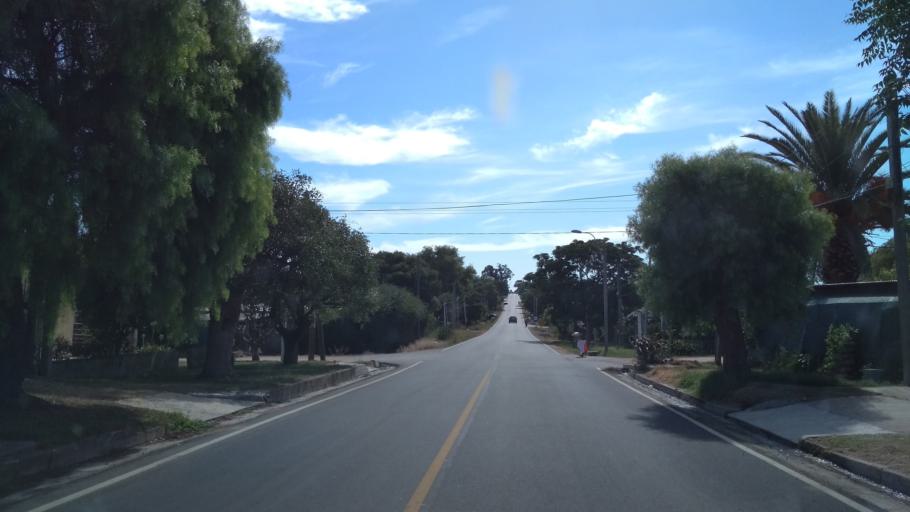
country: UY
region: Canelones
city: Joaquin Suarez
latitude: -34.7321
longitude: -56.0340
